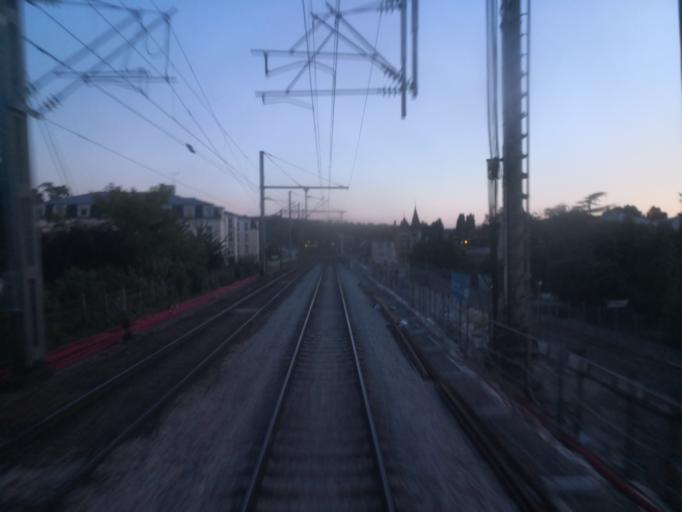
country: FR
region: Ile-de-France
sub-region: Departement des Yvelines
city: Poissy
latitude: 48.9317
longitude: 2.0376
